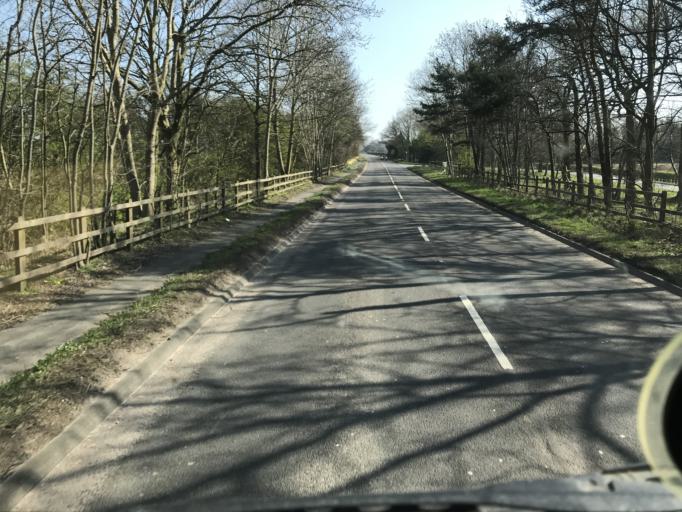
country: GB
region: England
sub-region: Cheshire East
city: Knutsford
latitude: 53.3027
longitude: -2.3993
